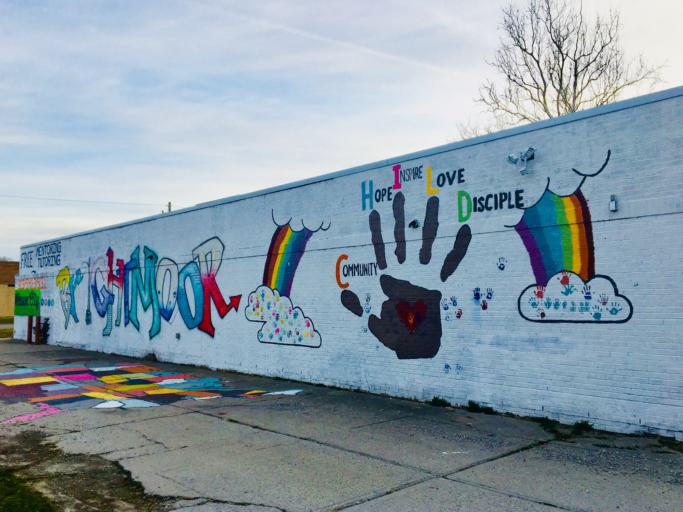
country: US
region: Michigan
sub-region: Wayne County
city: Redford
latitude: 42.3857
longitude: -83.2415
